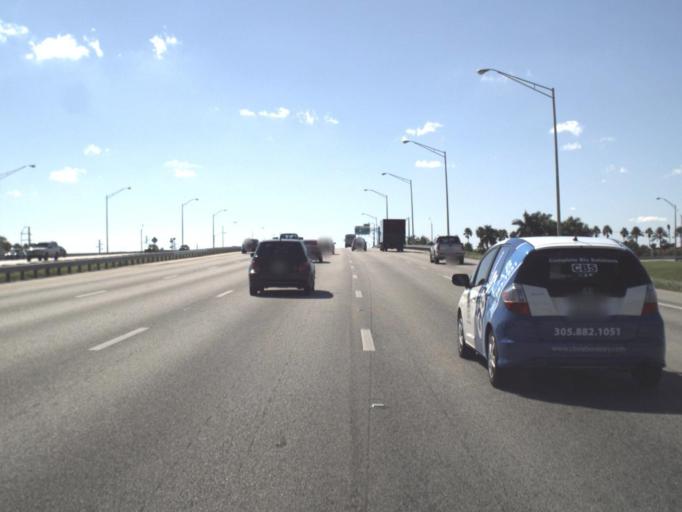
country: US
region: Florida
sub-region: Miami-Dade County
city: Sweetwater
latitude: 25.7637
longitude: -80.3856
